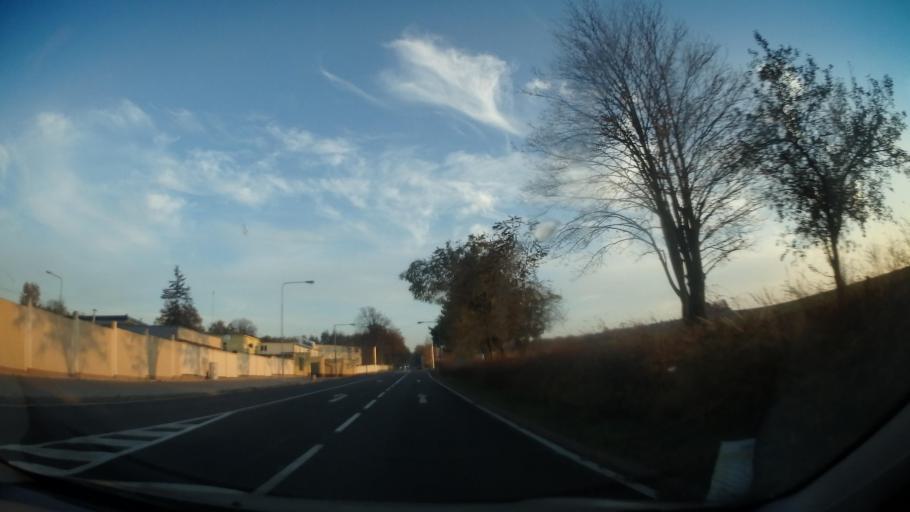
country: CZ
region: Central Bohemia
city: Vlasim
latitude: 49.6950
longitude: 14.9080
